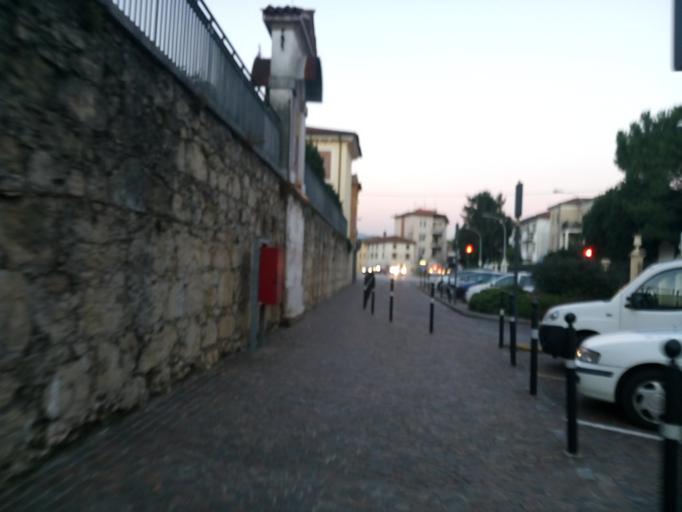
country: IT
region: Veneto
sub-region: Provincia di Vicenza
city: Schio
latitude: 45.7138
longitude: 11.3629
